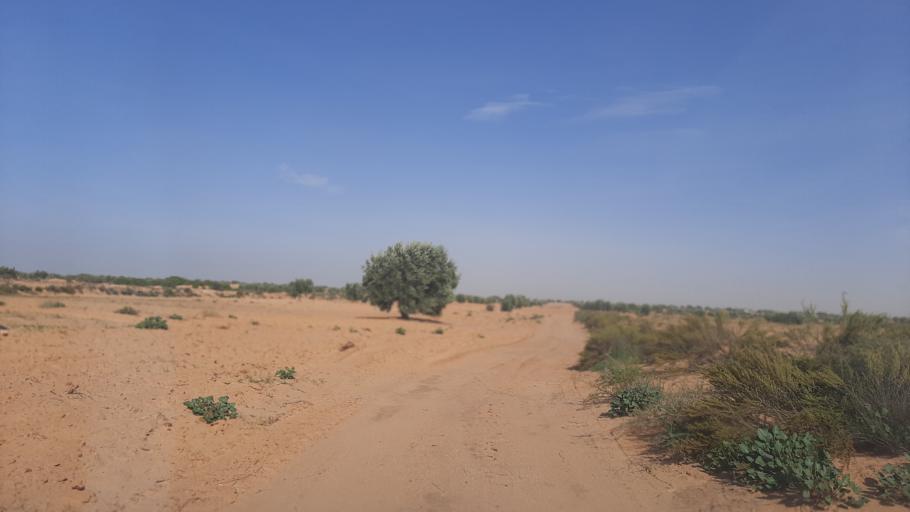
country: TN
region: Madanin
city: Zarzis
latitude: 33.4535
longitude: 10.8087
